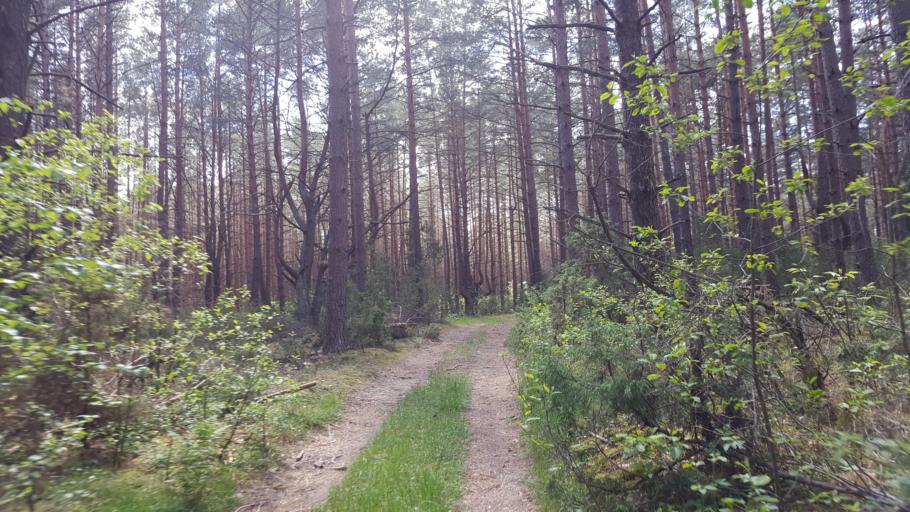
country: BY
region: Brest
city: Kamyanyets
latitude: 52.4486
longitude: 24.0070
